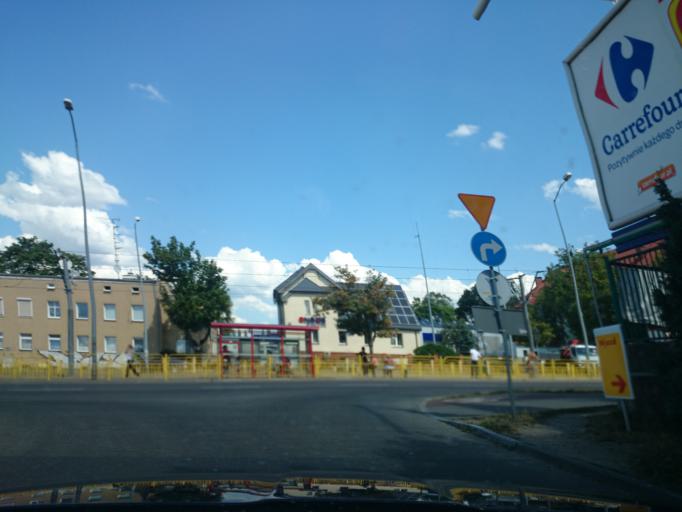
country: PL
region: West Pomeranian Voivodeship
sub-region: Szczecin
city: Szczecin
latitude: 53.4211
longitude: 14.5012
